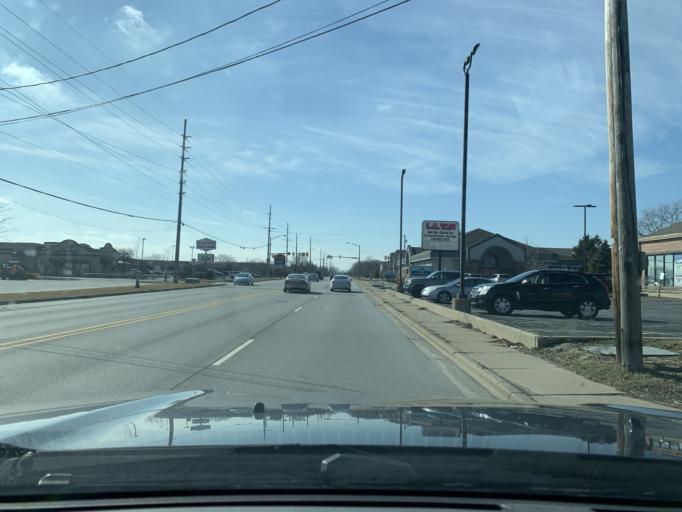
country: US
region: Indiana
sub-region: Lake County
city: Highland
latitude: 41.5376
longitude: -87.4743
